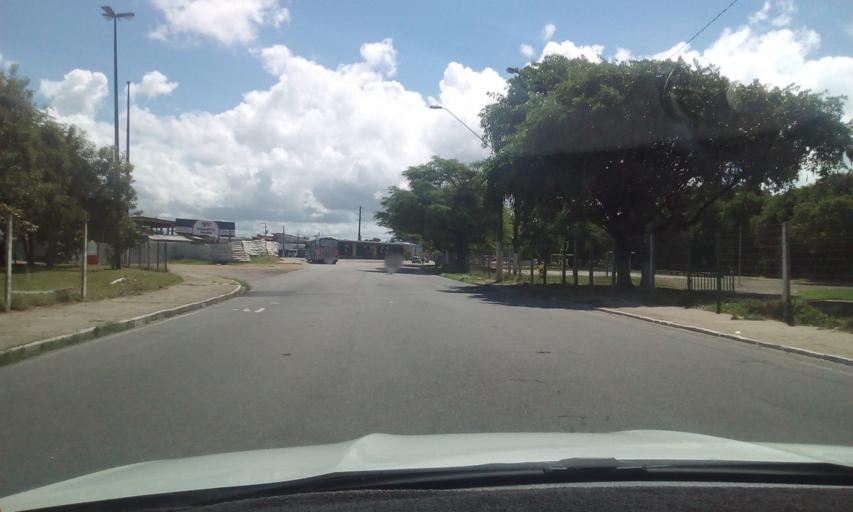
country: BR
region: Pernambuco
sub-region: Olinda
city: Olinda
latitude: -8.0291
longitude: -34.8646
